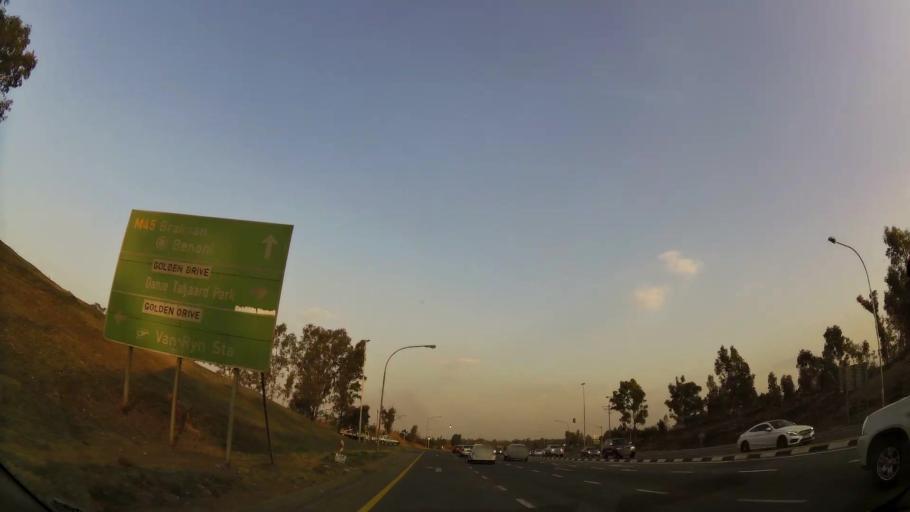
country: ZA
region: Gauteng
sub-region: Ekurhuleni Metropolitan Municipality
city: Benoni
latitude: -26.1774
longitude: 28.3349
